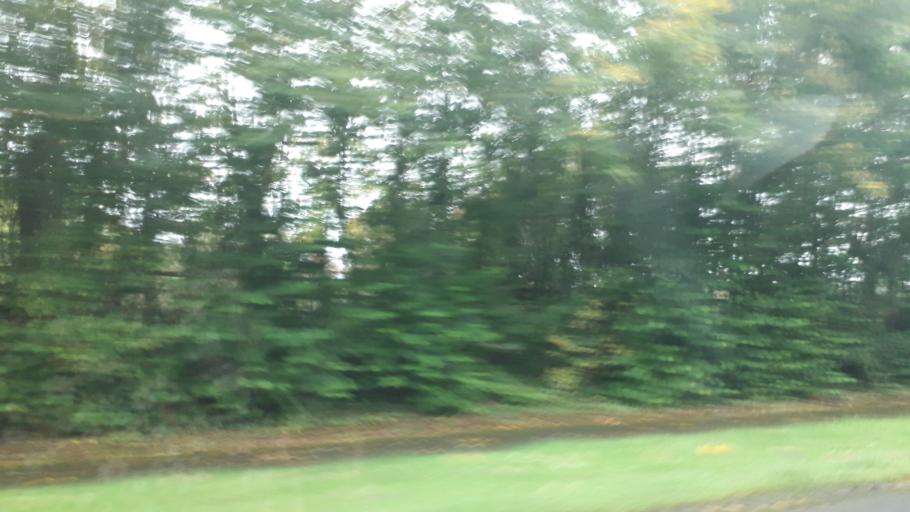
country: IE
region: Leinster
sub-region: An Longfort
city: Longford
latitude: 53.7407
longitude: -7.7824
